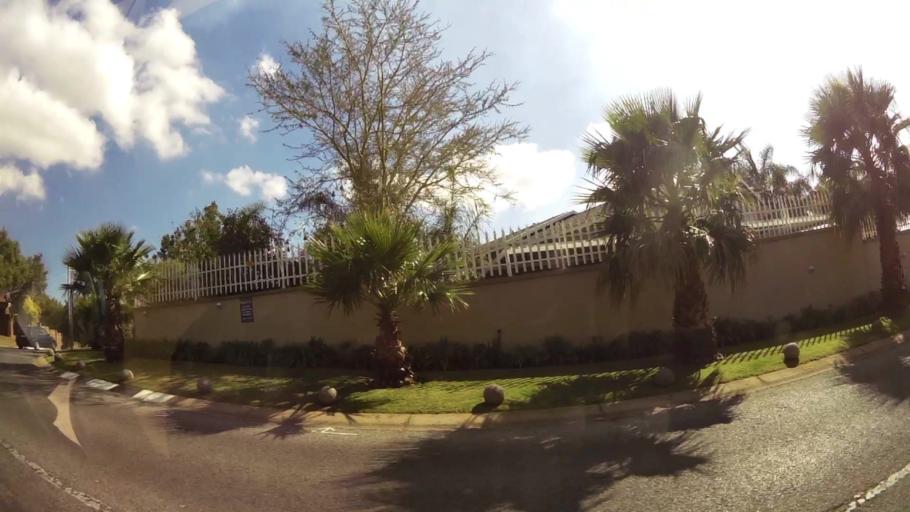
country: ZA
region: Gauteng
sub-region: City of Johannesburg Metropolitan Municipality
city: Roodepoort
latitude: -26.1171
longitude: 27.8409
